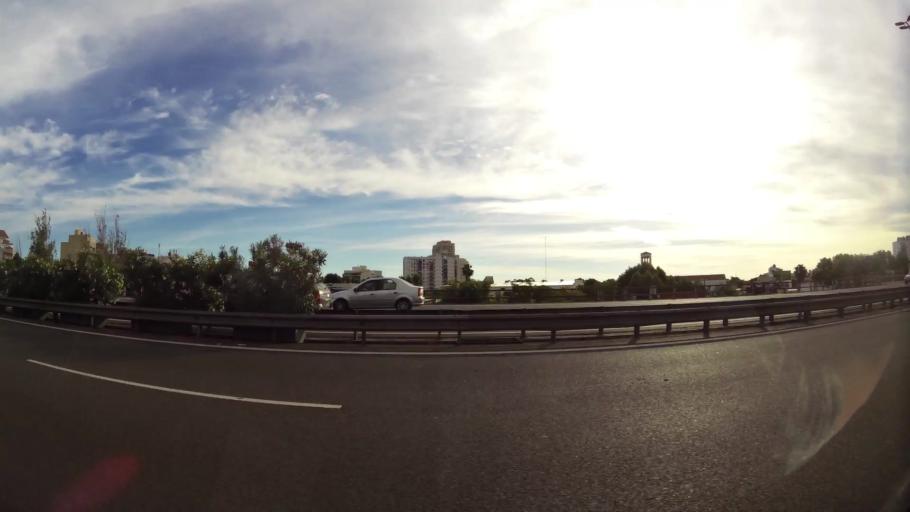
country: AR
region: Buenos Aires F.D.
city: Villa Santa Rita
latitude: -34.6411
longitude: -58.4919
